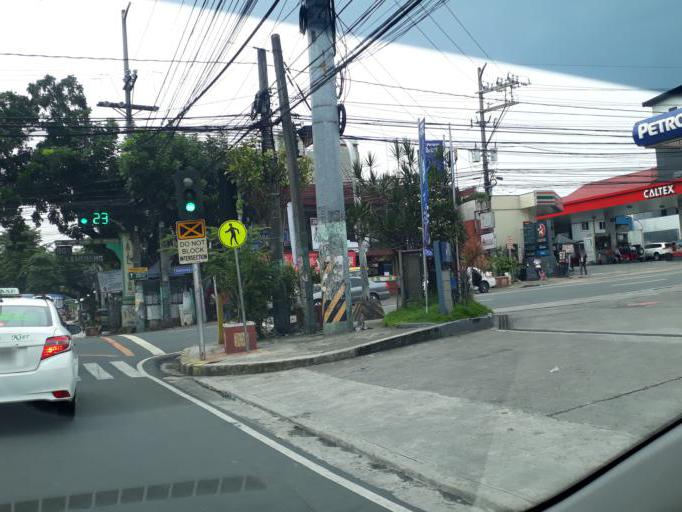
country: PH
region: Metro Manila
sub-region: Quezon City
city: Quezon City
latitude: 14.6289
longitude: 121.0386
